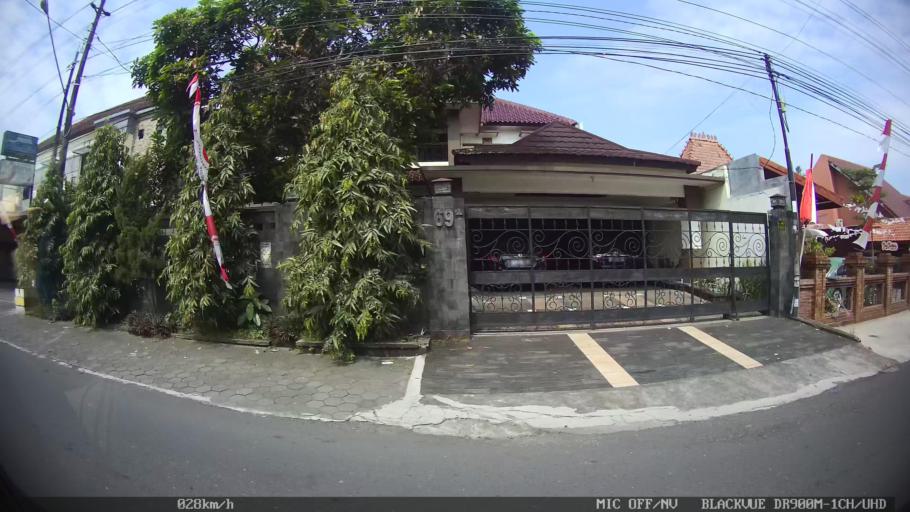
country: ID
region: Daerah Istimewa Yogyakarta
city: Depok
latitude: -7.7718
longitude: 110.4380
